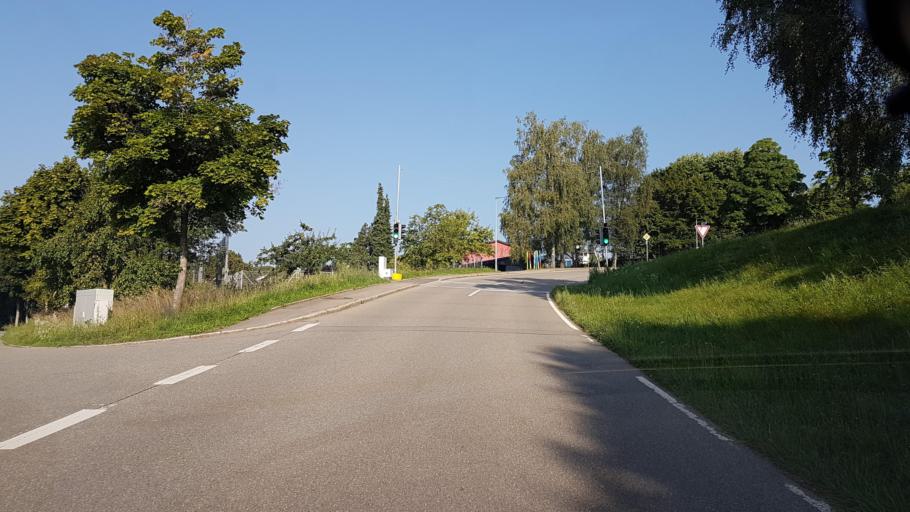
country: DE
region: Baden-Wuerttemberg
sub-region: Freiburg Region
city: Albbruck
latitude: 47.6154
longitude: 8.1086
